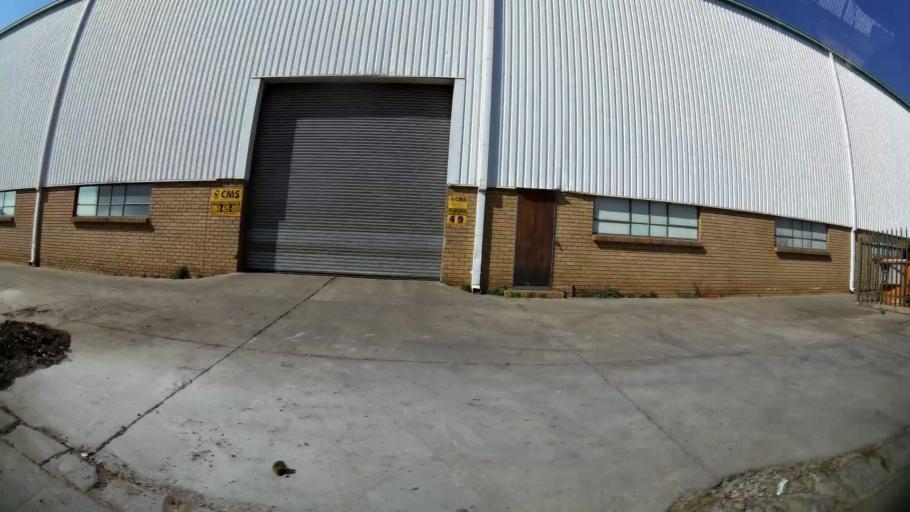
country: ZA
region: Gauteng
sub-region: Ekurhuleni Metropolitan Municipality
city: Boksburg
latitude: -26.1733
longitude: 28.2282
